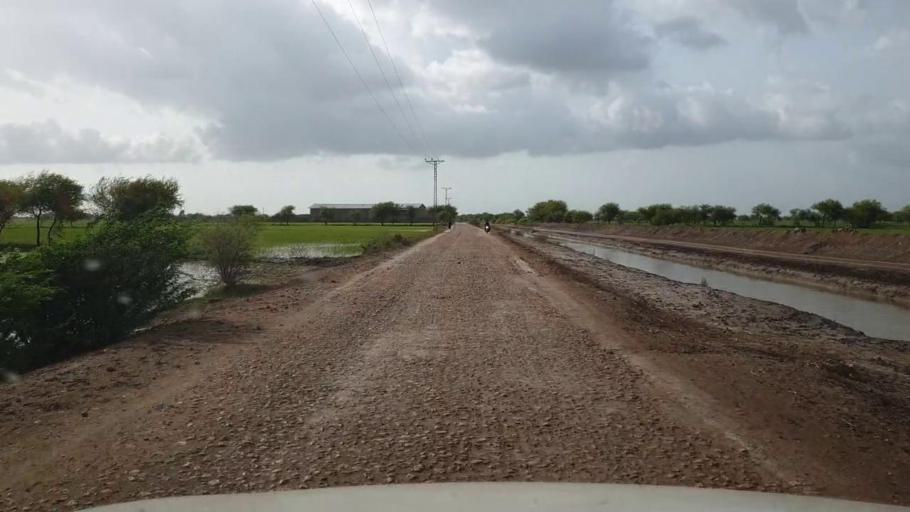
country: PK
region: Sindh
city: Kario
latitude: 24.7819
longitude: 68.5876
